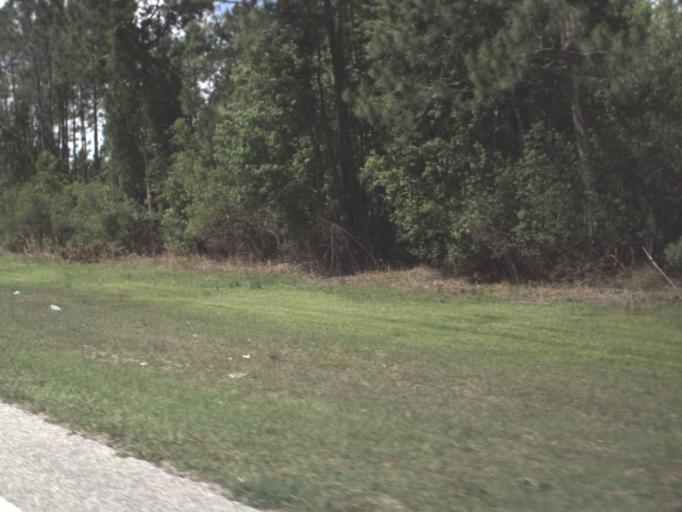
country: US
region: Florida
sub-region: Flagler County
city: Palm Coast
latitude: 29.5448
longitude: -81.2644
